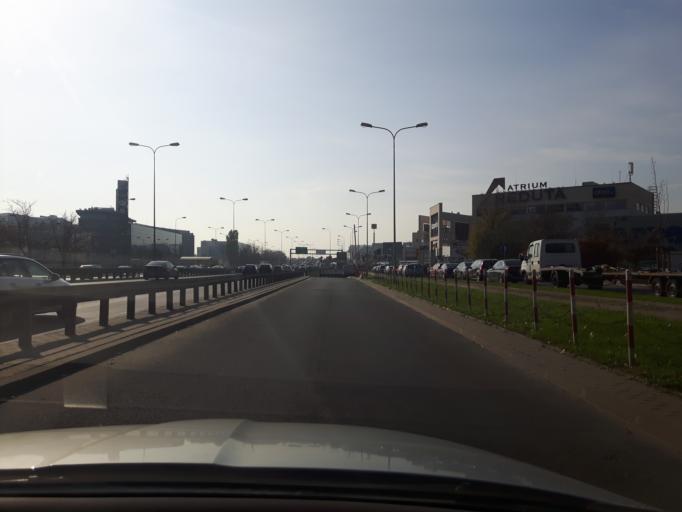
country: PL
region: Masovian Voivodeship
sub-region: Warszawa
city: Ochota
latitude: 52.2135
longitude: 20.9542
